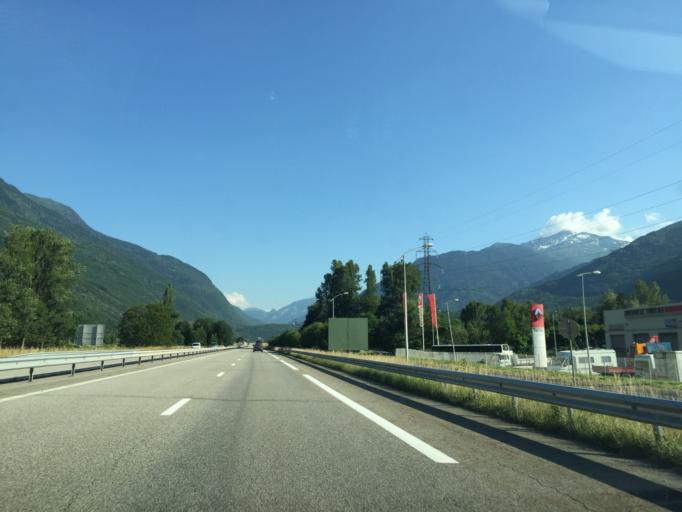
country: FR
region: Rhone-Alpes
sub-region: Departement de la Savoie
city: La Bathie
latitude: 45.6367
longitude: 6.4414
